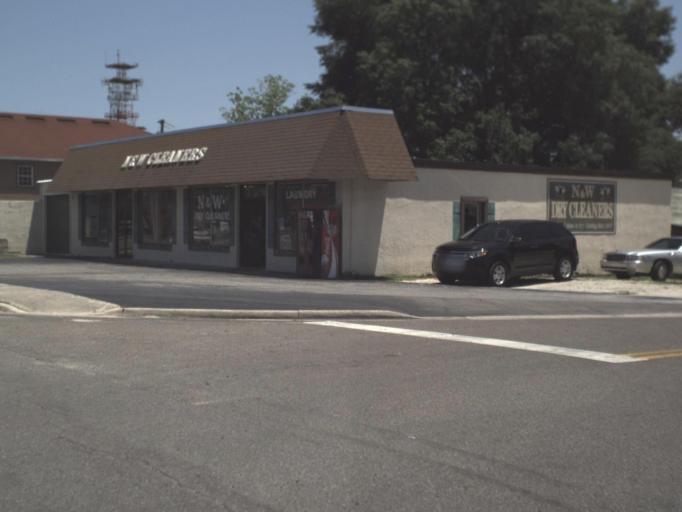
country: US
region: Florida
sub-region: Columbia County
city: Lake City
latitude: 30.1893
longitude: -82.6411
